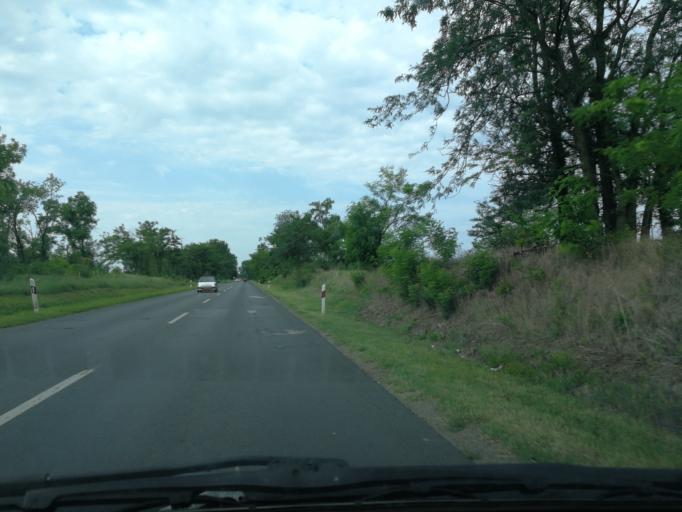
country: HU
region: Bacs-Kiskun
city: Ersekcsanad
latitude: 46.2222
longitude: 18.9659
